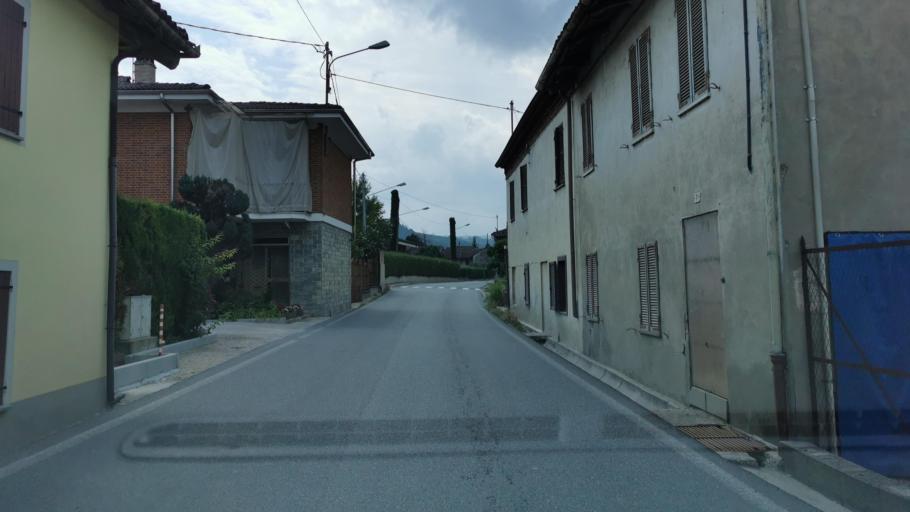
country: IT
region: Piedmont
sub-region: Provincia di Cuneo
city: Grinzane Cavour
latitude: 44.6454
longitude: 7.9980
